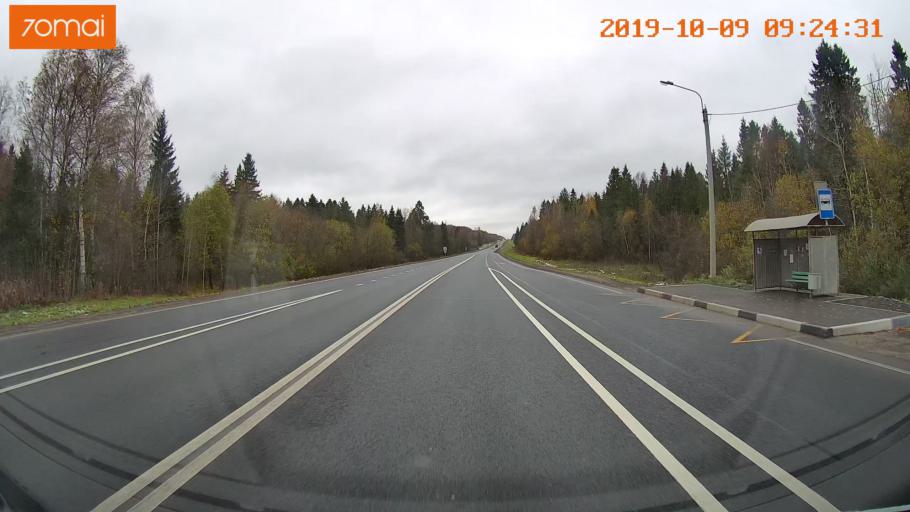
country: RU
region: Vologda
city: Vologda
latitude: 59.0798
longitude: 40.0150
